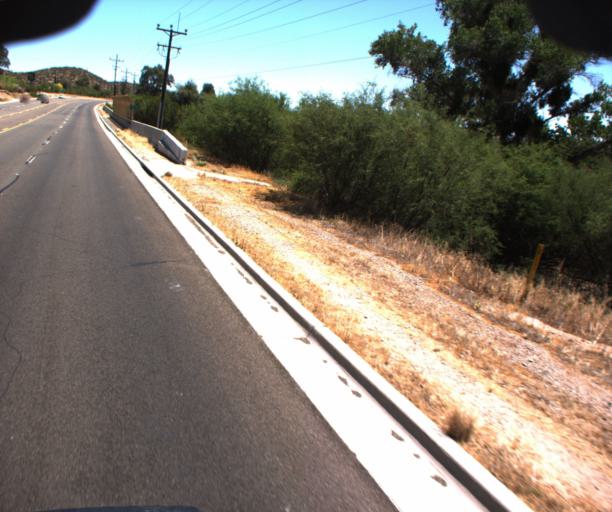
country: US
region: Arizona
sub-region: Maricopa County
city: Wickenburg
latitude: 33.9633
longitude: -112.7169
